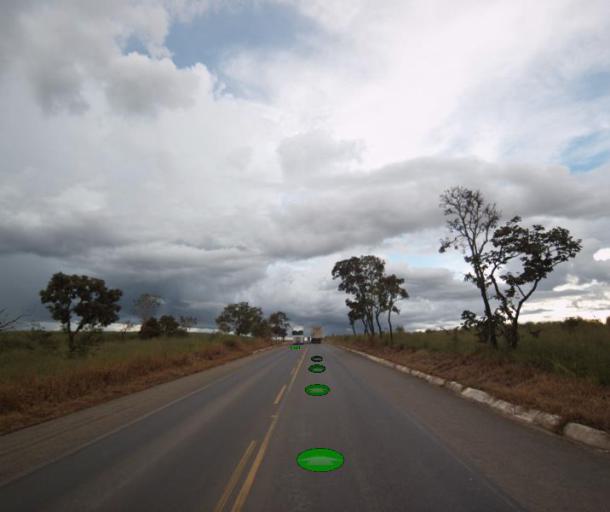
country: BR
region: Goias
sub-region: Itapaci
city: Itapaci
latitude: -14.8041
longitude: -49.2872
